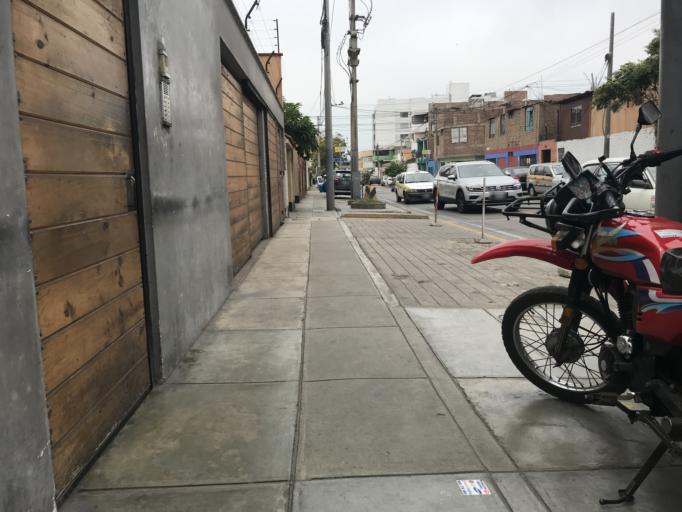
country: PE
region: Lima
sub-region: Lima
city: San Isidro
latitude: -12.0837
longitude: -77.0744
